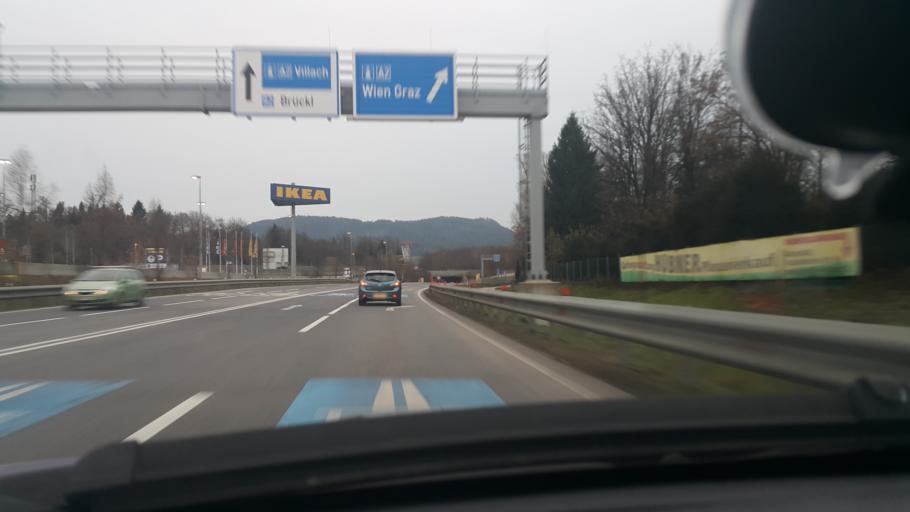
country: AT
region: Carinthia
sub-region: Politischer Bezirk Klagenfurt Land
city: Ebenthal
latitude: 46.6391
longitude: 14.3705
